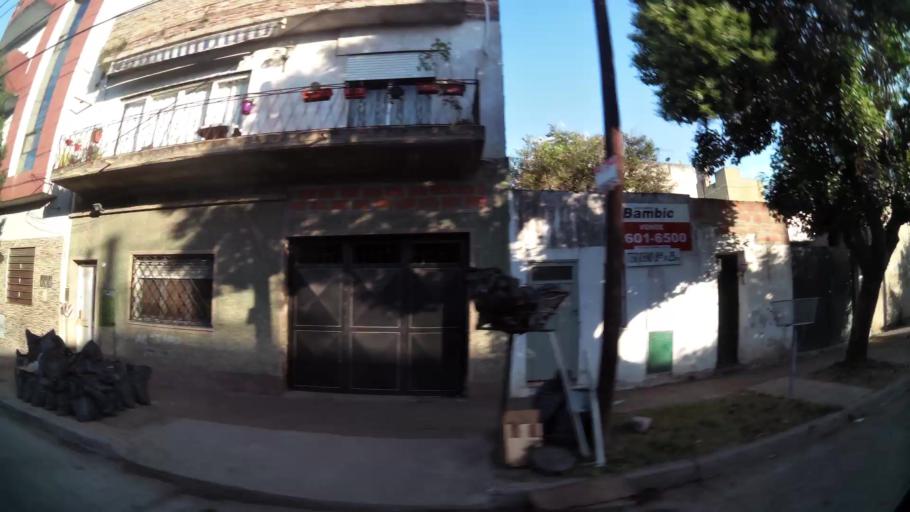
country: AR
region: Buenos Aires F.D.
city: Villa Lugano
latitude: -34.6916
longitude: -58.4841
